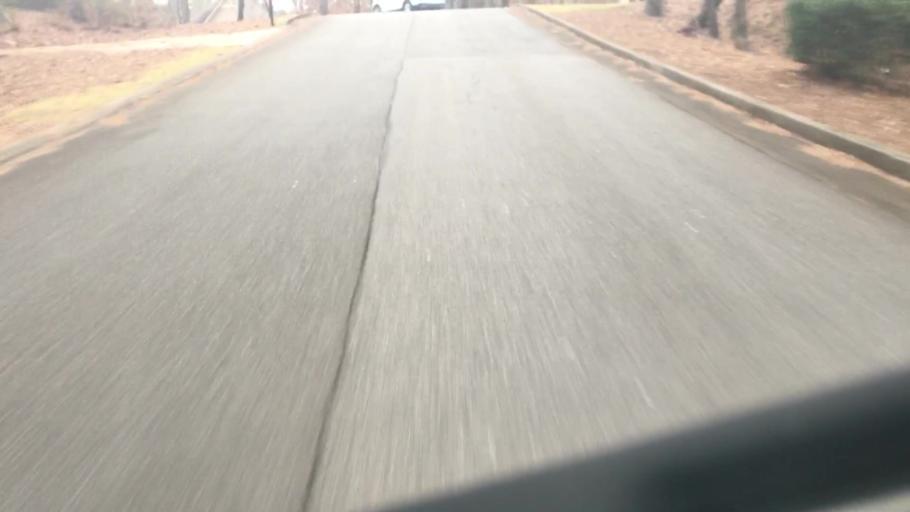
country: US
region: Alabama
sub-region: Shelby County
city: Helena
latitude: 33.3451
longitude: -86.8190
